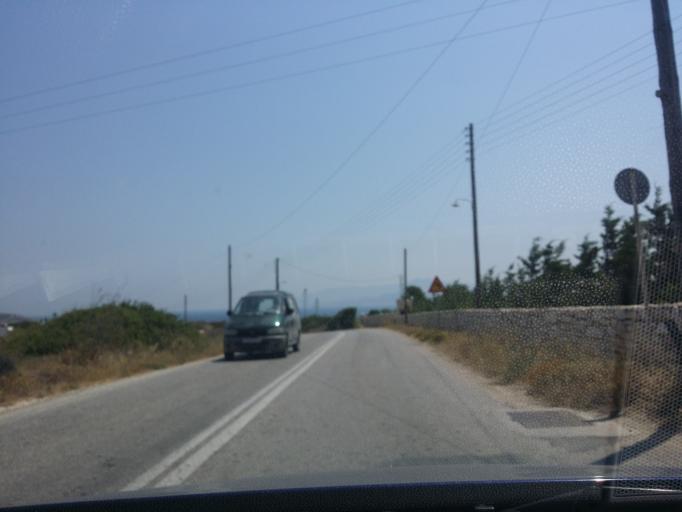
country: GR
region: South Aegean
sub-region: Nomos Kykladon
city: Naousa
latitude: 37.0669
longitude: 25.2416
